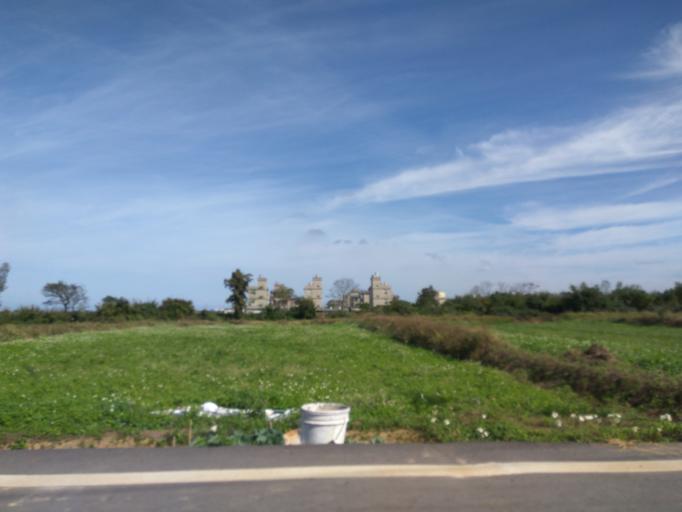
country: TW
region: Taiwan
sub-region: Hsinchu
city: Zhubei
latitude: 25.0146
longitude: 121.0896
